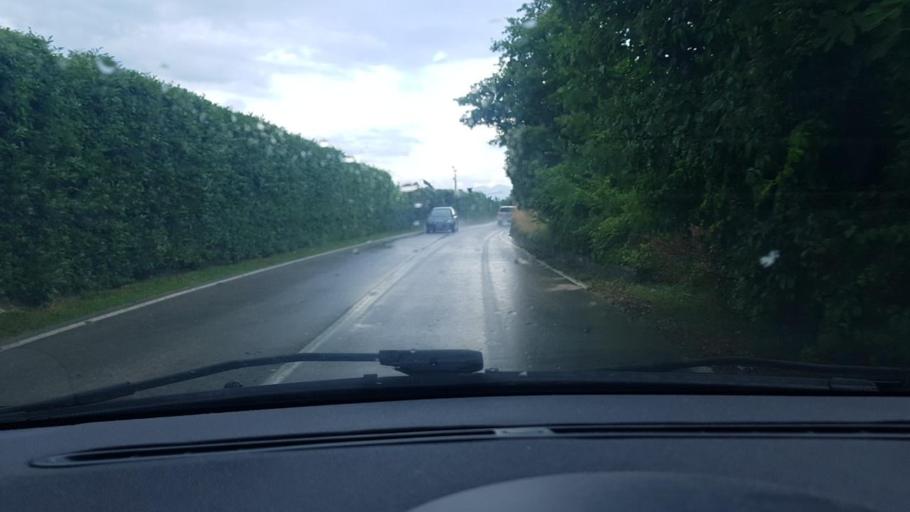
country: IT
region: Veneto
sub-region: Provincia di Verona
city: Torri del Benaco
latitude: 45.5996
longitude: 10.7001
